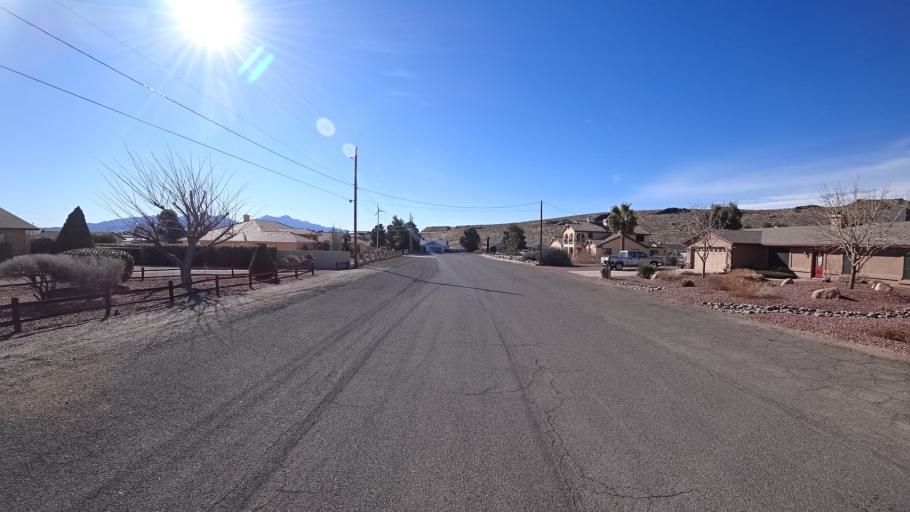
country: US
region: Arizona
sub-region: Mohave County
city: New Kingman-Butler
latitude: 35.2603
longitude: -114.0410
